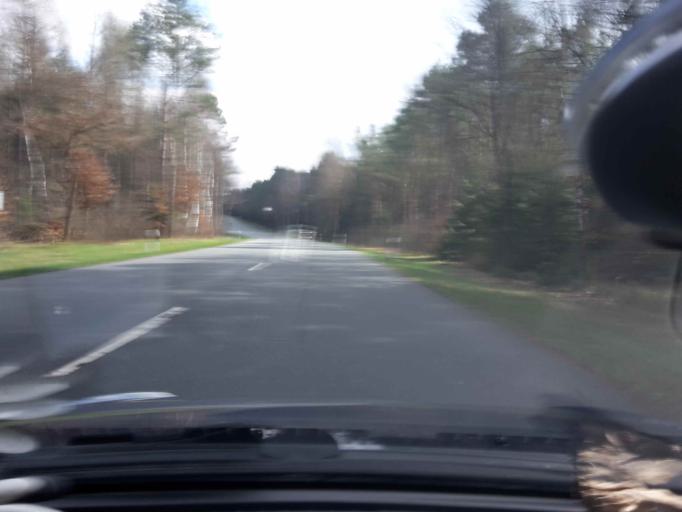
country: DE
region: Lower Saxony
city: Bispingen
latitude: 53.0497
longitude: 10.0354
